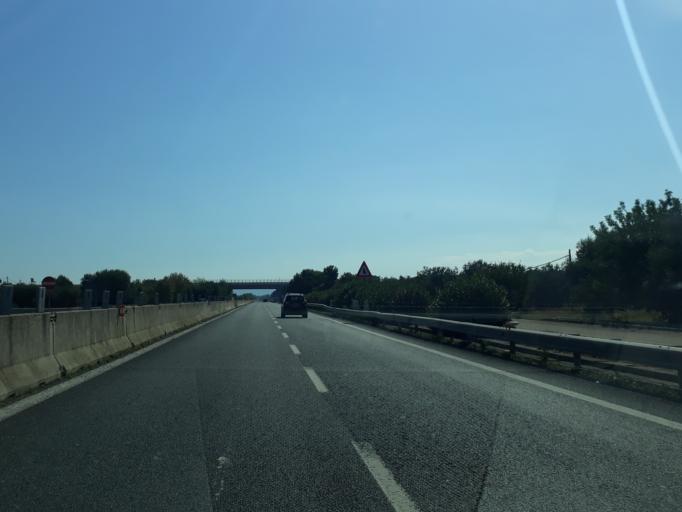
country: IT
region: Apulia
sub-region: Provincia di Bari
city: Monopoli
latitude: 40.9093
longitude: 17.3231
